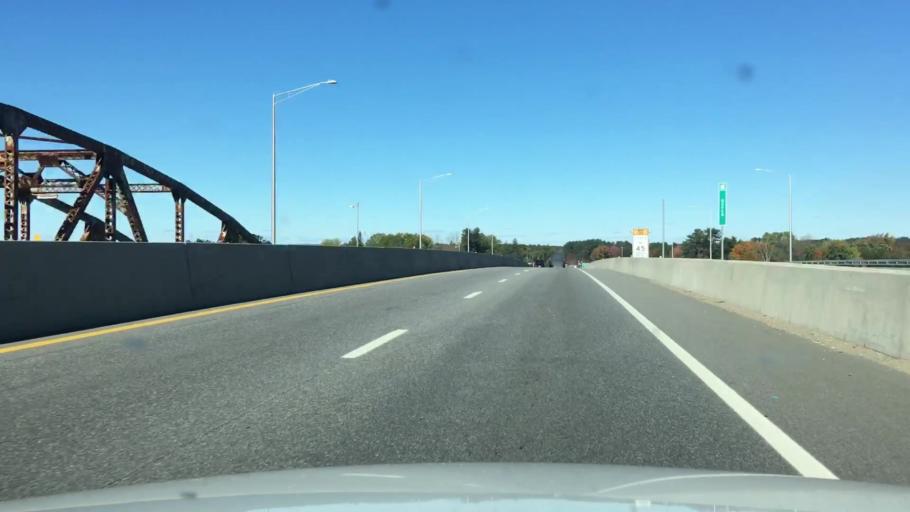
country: US
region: Maine
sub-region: York County
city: Eliot
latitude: 43.1181
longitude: -70.8258
